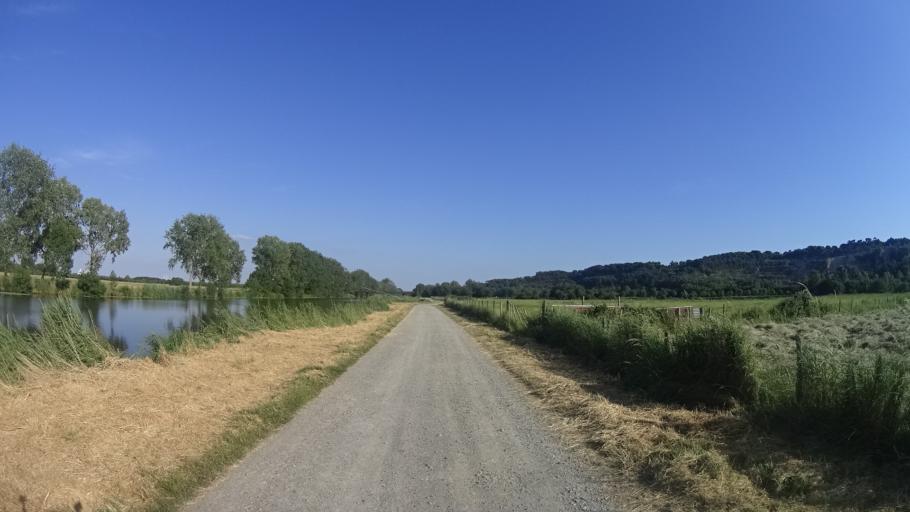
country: FR
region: Brittany
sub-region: Departement du Morbihan
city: Saint-Jean-la-Poterie
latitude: 47.6444
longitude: -2.1110
